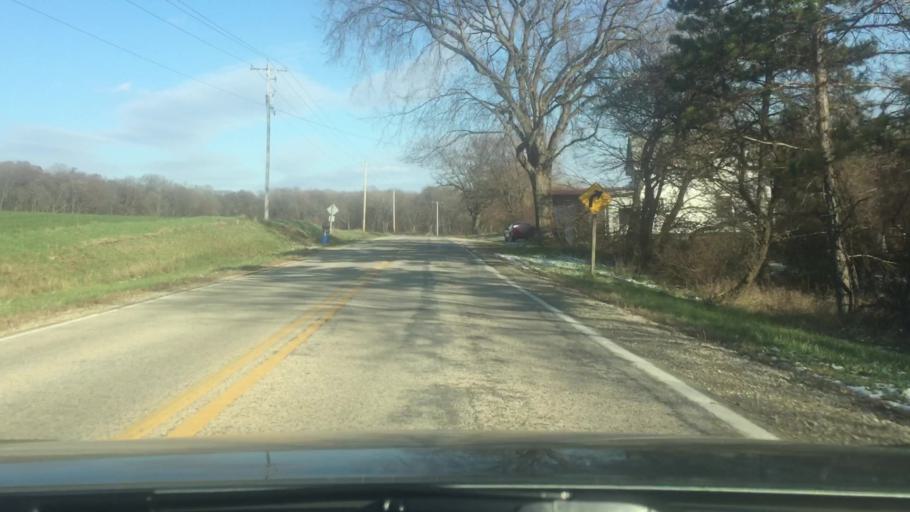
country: US
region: Wisconsin
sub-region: Jefferson County
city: Palmyra
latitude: 42.9391
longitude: -88.6096
